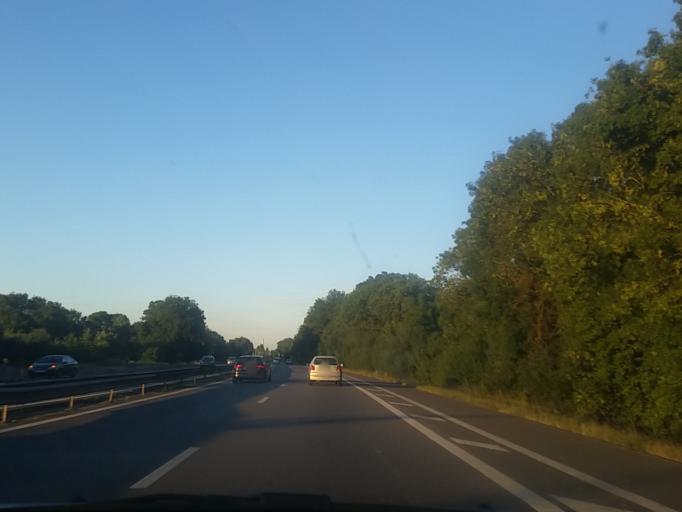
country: FR
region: Pays de la Loire
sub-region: Departement de la Loire-Atlantique
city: Reze
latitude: 47.1885
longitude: -1.5847
